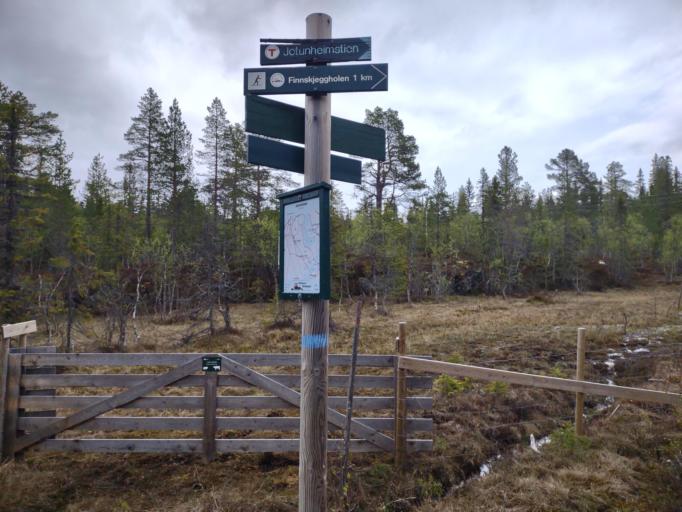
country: NO
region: Oppland
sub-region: Gran
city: Jaren
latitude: 60.4477
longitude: 10.6486
